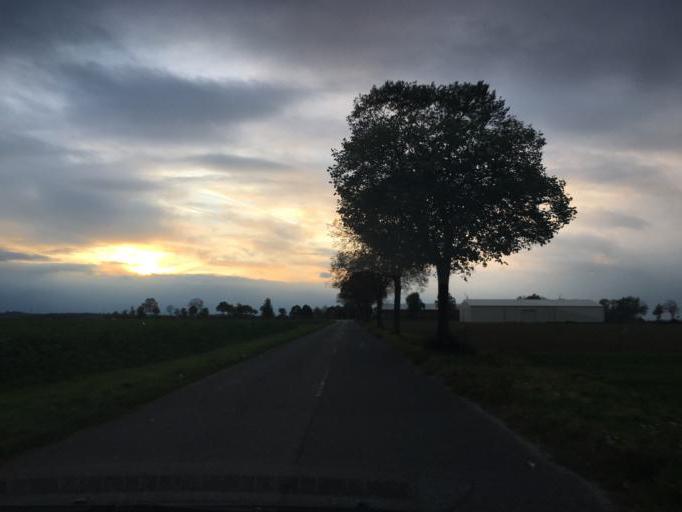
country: DE
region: North Rhine-Westphalia
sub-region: Regierungsbezirk Koln
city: Norvenich
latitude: 50.7662
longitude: 6.7092
